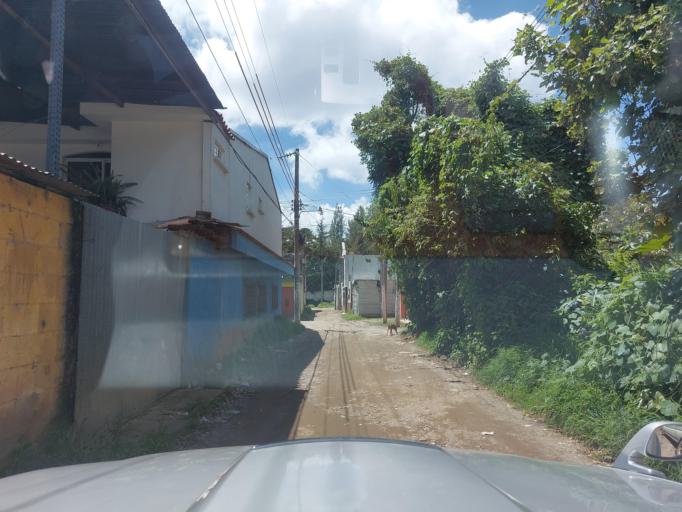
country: GT
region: Chimaltenango
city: El Tejar
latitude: 14.6414
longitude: -90.8119
